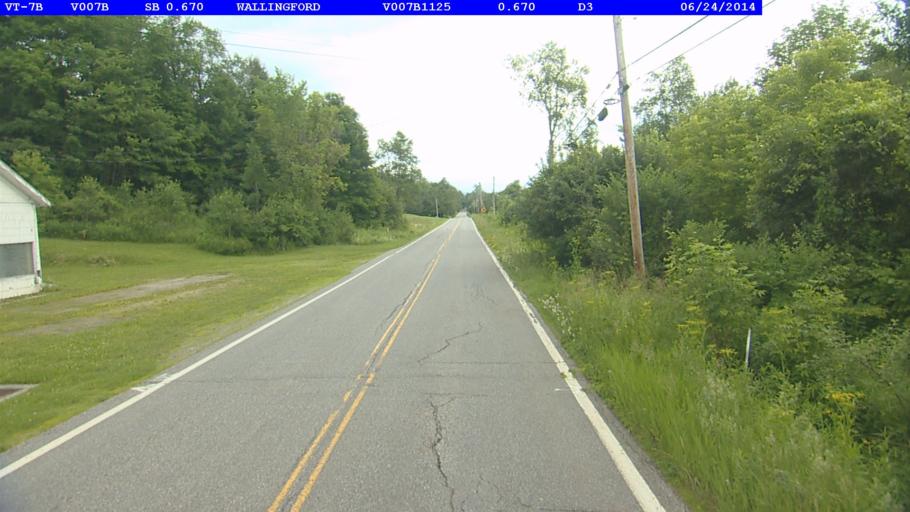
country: US
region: Vermont
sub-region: Rutland County
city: Rutland
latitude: 43.4939
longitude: -72.9726
